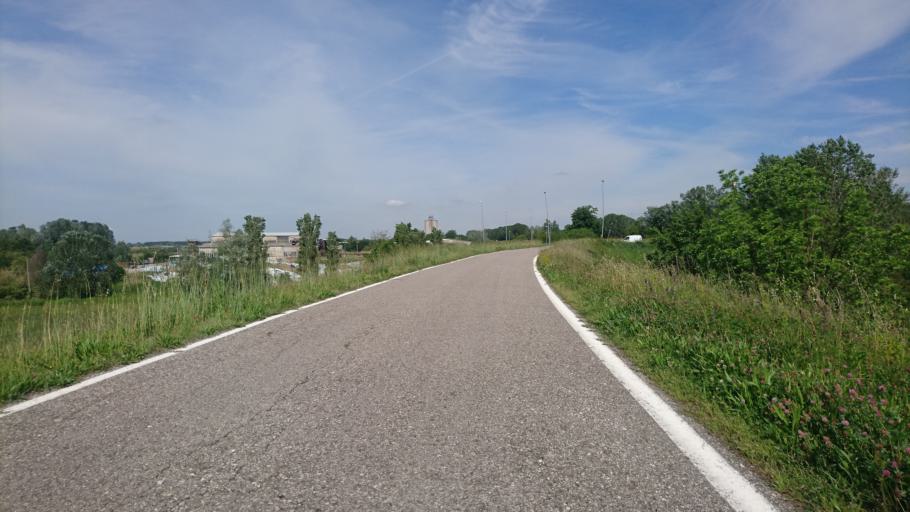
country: IT
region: Lombardy
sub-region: Provincia di Mantova
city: Revere
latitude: 45.0432
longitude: 11.1495
